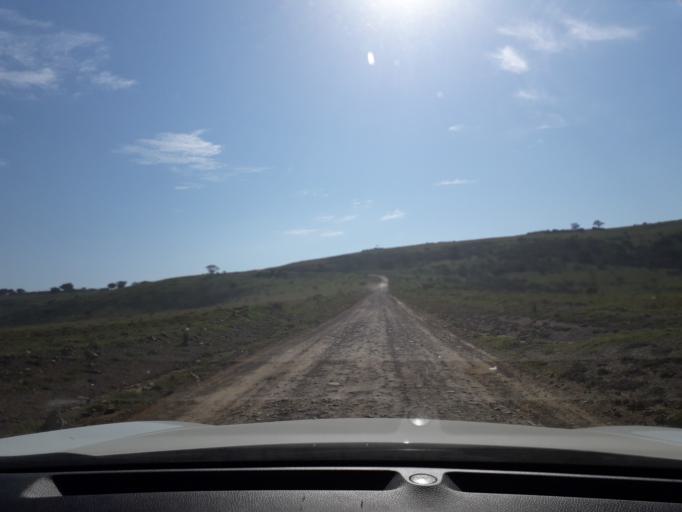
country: ZA
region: Eastern Cape
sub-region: Buffalo City Metropolitan Municipality
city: Bhisho
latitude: -32.9808
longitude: 27.3230
